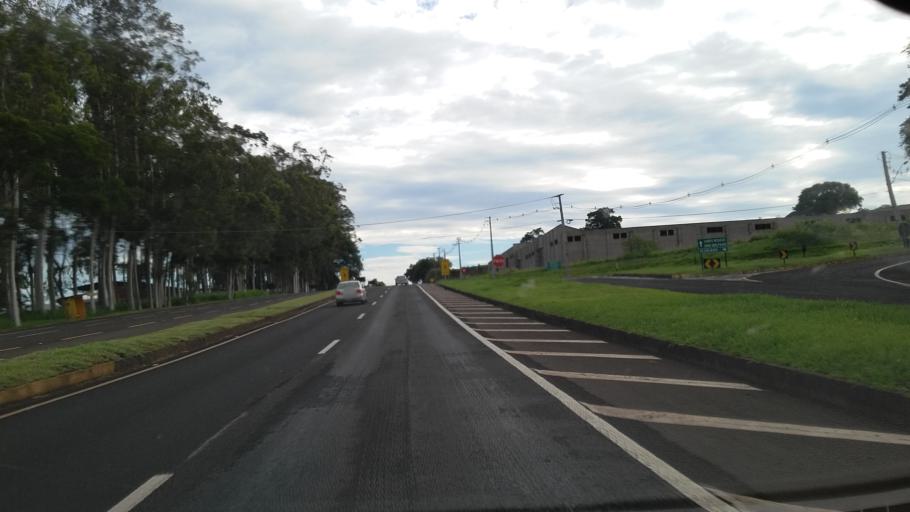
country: BR
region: Parana
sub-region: Paicandu
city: Paicandu
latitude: -23.5217
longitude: -52.0297
